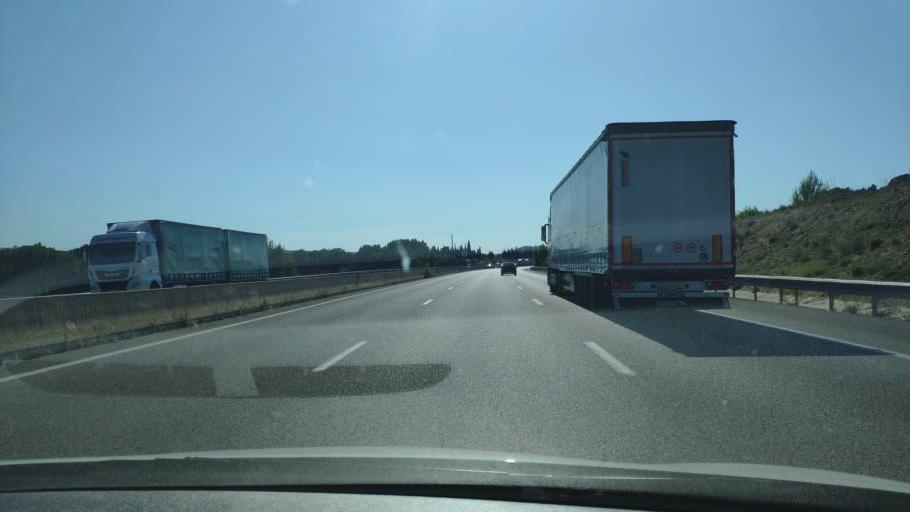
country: FR
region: Provence-Alpes-Cote d'Azur
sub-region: Departement des Bouches-du-Rhone
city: Chateauneuf-le-Rouge
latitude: 43.4802
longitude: 5.5864
